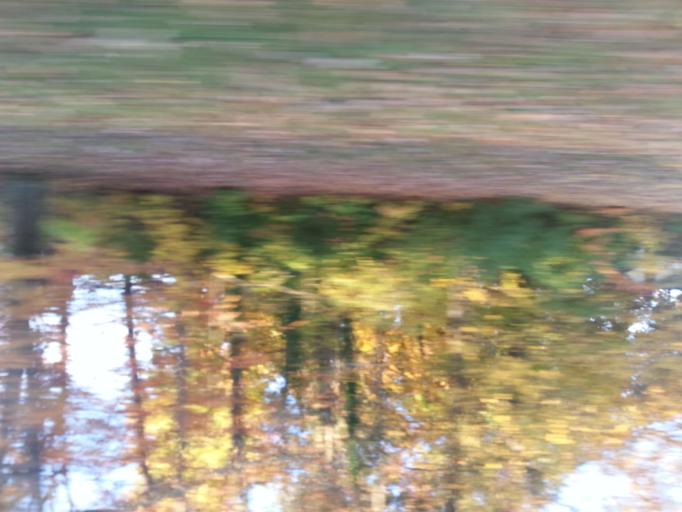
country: US
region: Tennessee
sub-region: Blount County
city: Louisville
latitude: 35.9101
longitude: -84.0361
